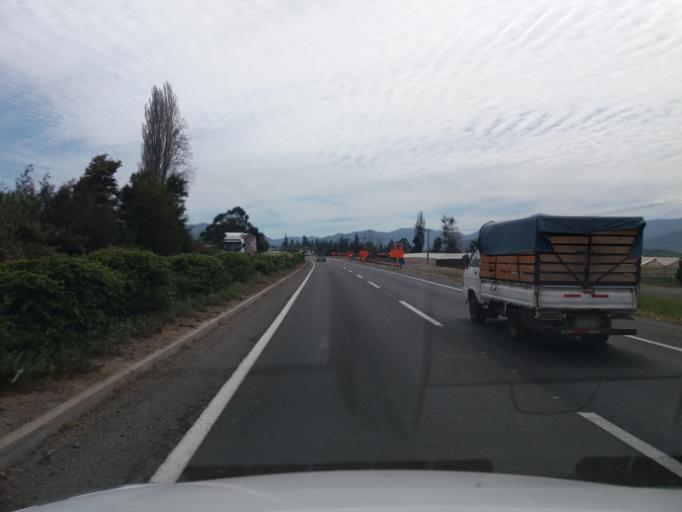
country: CL
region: Valparaiso
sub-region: Provincia de Quillota
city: Hacienda La Calera
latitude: -32.7415
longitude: -71.1980
